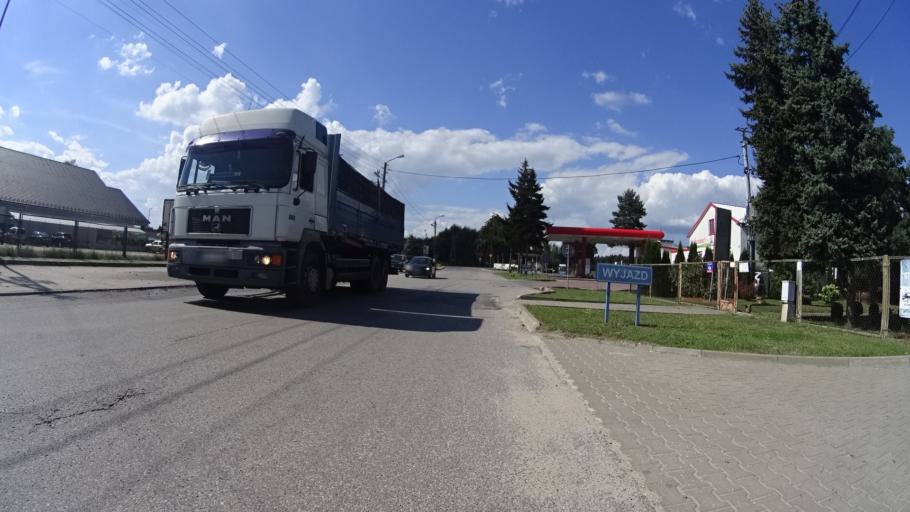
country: PL
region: Masovian Voivodeship
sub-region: Powiat grojecki
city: Mogielnica
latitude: 51.6960
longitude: 20.7280
